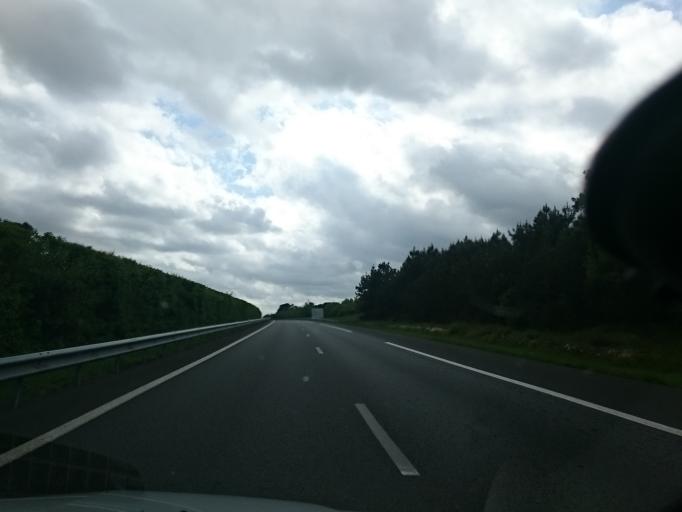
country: FR
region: Brittany
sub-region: Departement d'Ille-et-Vilaine
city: Gosne
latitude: 48.2323
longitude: -1.4849
